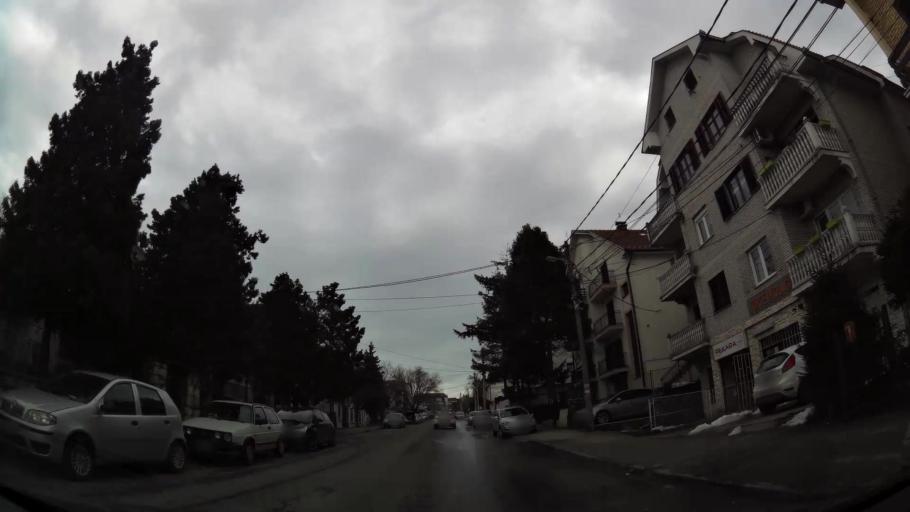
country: RS
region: Central Serbia
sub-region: Belgrade
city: Cukarica
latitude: 44.7544
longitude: 20.4107
